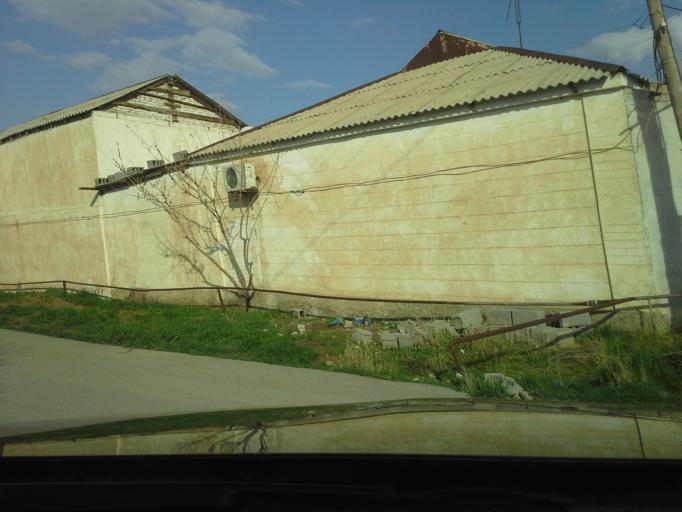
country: TM
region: Ahal
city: Abadan
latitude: 38.0140
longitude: 58.2306
